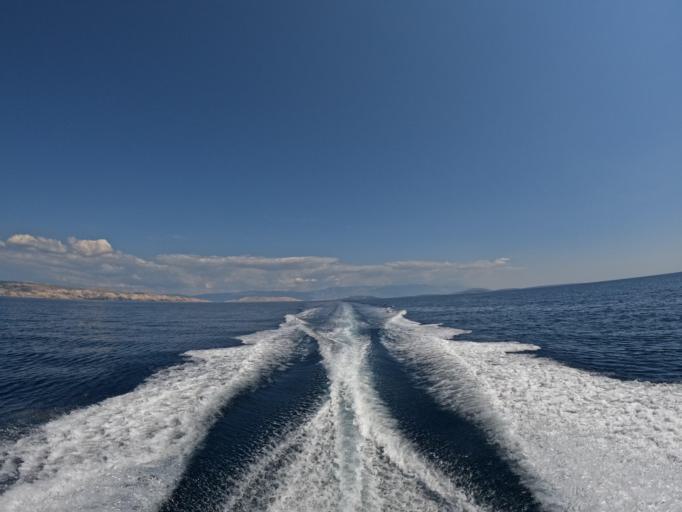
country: HR
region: Primorsko-Goranska
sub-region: Grad Krk
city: Krk
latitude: 44.9217
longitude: 14.5586
